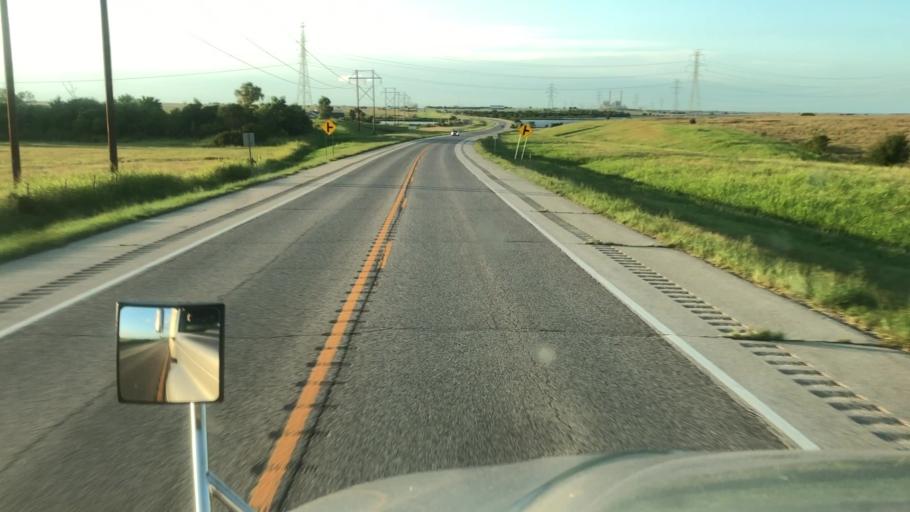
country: US
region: Oklahoma
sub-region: Noble County
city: Perry
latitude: 36.3989
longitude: -97.0676
